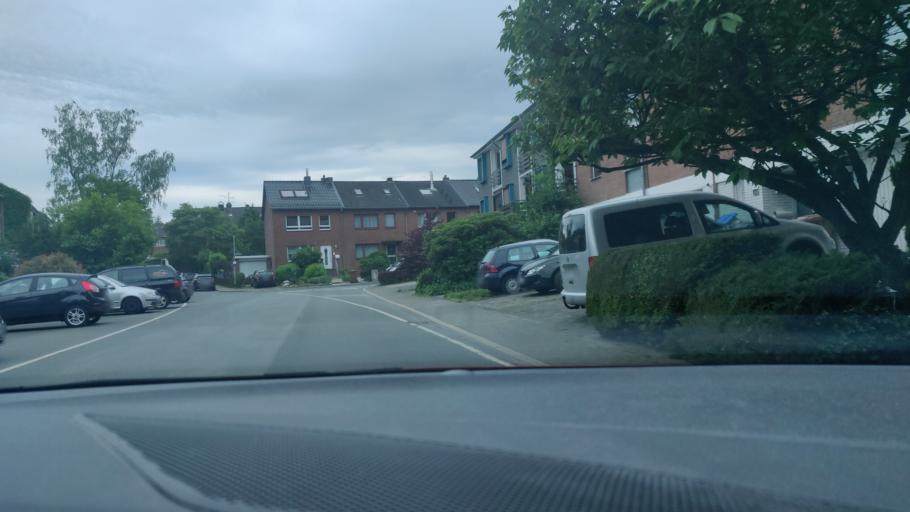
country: DE
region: North Rhine-Westphalia
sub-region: Regierungsbezirk Dusseldorf
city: Heiligenhaus
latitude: 51.2985
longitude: 6.9186
